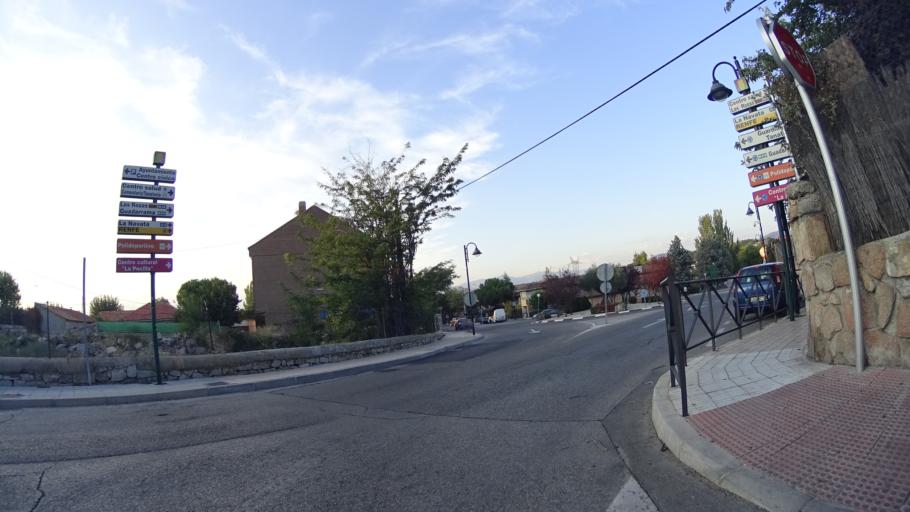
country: ES
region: Madrid
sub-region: Provincia de Madrid
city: Galapagar
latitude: 40.5811
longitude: -4.0001
